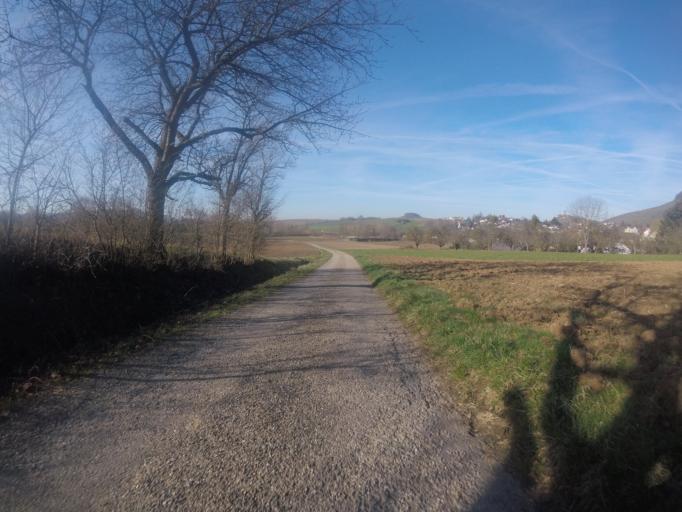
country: DE
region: Baden-Wuerttemberg
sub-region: Regierungsbezirk Stuttgart
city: Oberstenfeld
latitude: 49.0406
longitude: 9.3364
